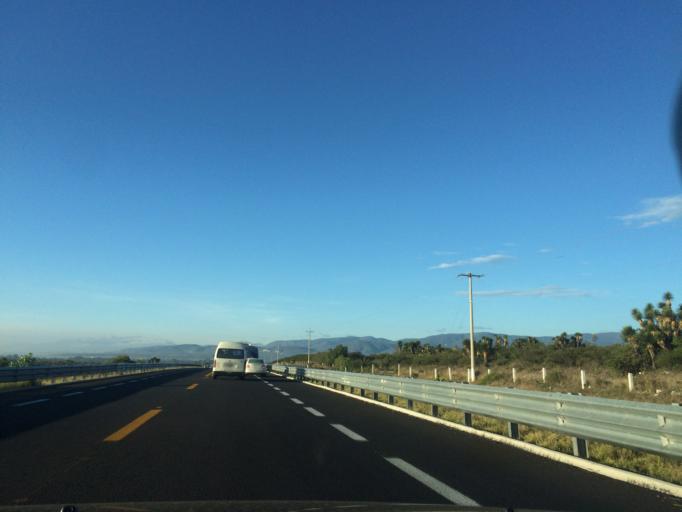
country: MX
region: Puebla
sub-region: Tehuacan
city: Magdalena Cuayucatepec
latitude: 18.5593
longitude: -97.4633
